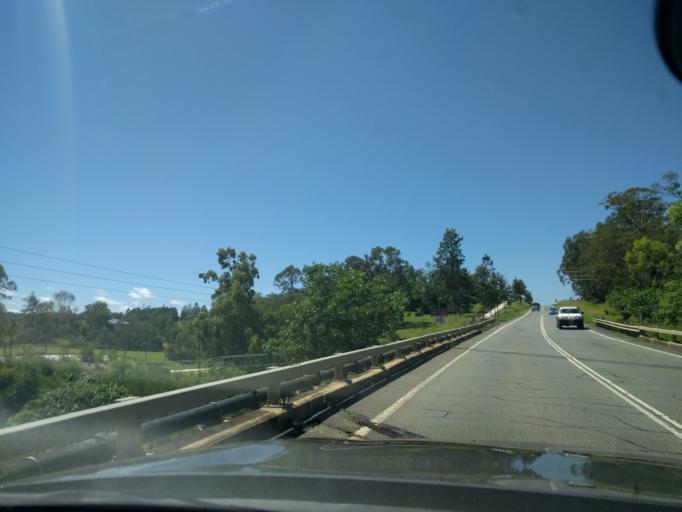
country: AU
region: Queensland
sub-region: Logan
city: Cedar Vale
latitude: -27.9633
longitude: 152.9955
